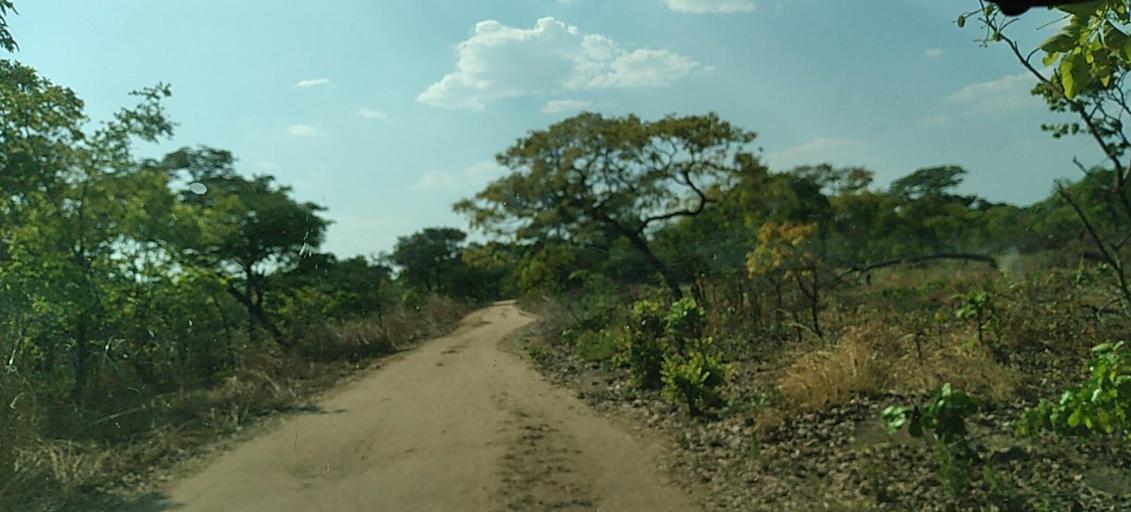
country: ZM
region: North-Western
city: Kalengwa
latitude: -13.1043
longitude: 24.9882
